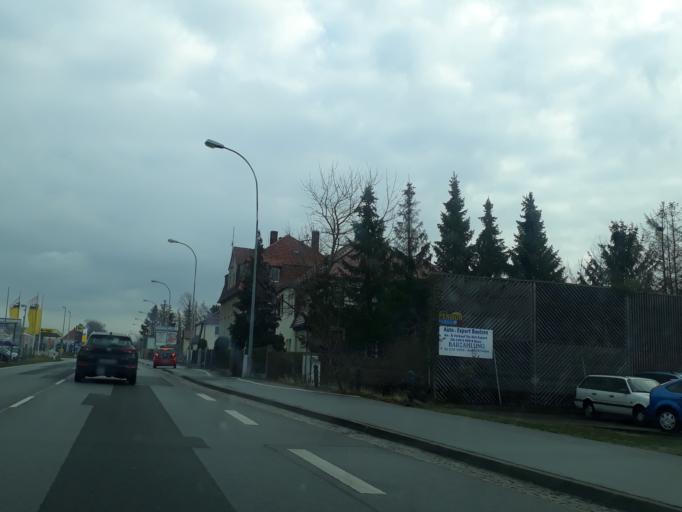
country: DE
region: Saxony
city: Kubschutz
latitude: 51.1731
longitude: 14.4723
